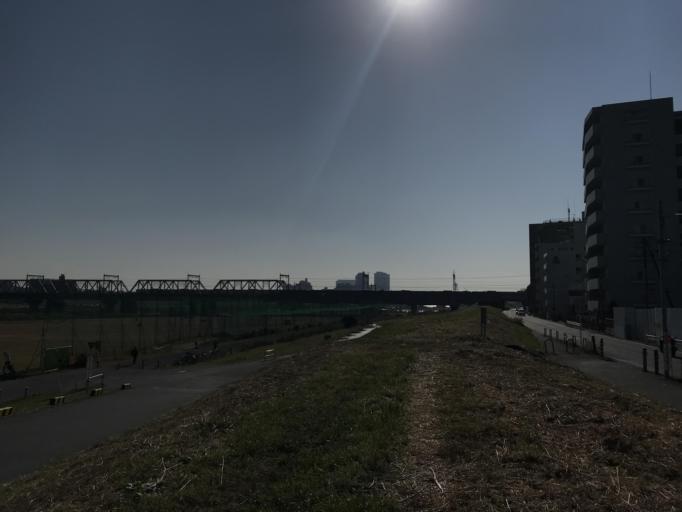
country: JP
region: Kanagawa
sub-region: Kawasaki-shi
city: Kawasaki
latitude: 35.5824
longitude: 139.6672
